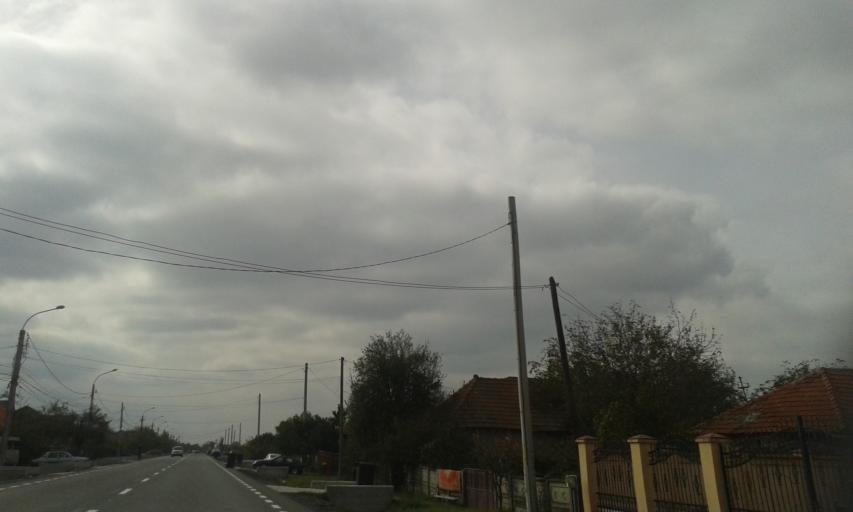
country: RO
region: Gorj
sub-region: Comuna Turcinesti
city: Turcinesti
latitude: 45.0970
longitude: 23.3314
